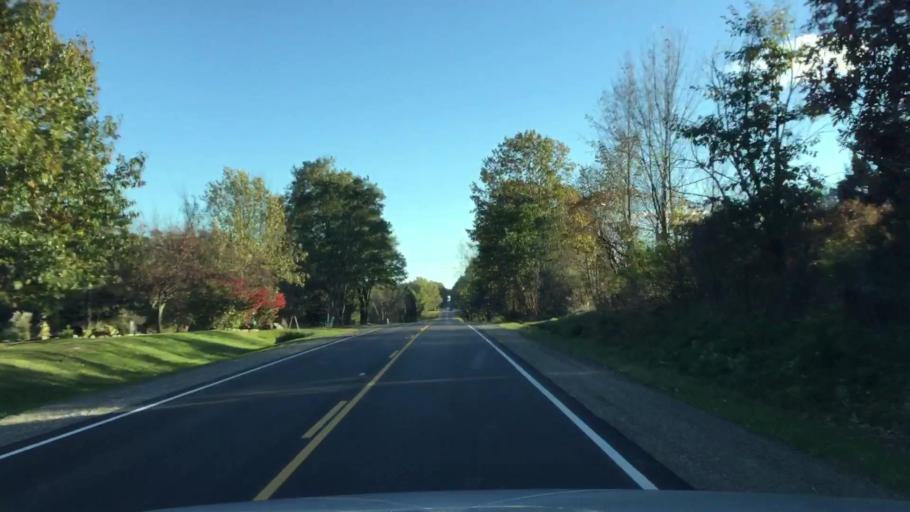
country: US
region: Michigan
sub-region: Lapeer County
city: Almont
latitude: 42.9255
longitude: -83.1438
